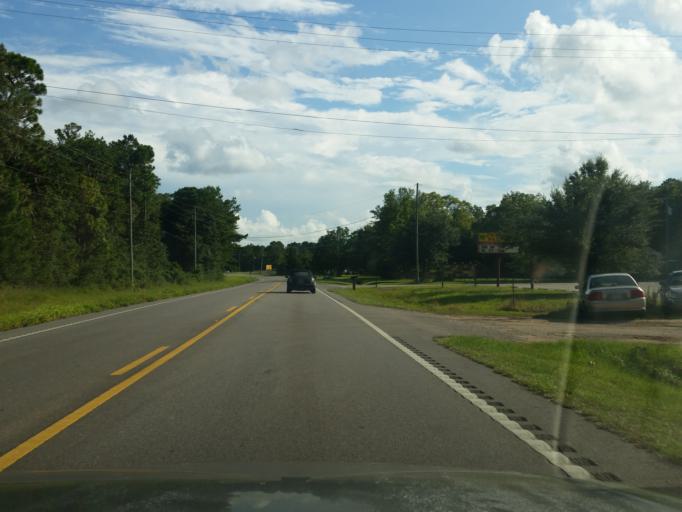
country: US
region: Alabama
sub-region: Mobile County
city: Theodore
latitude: 30.4499
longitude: -88.1162
